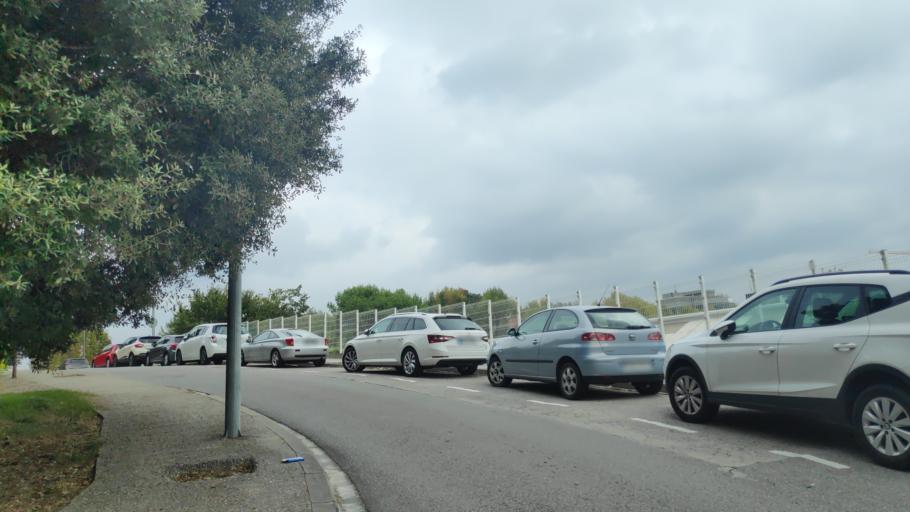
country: ES
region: Catalonia
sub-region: Provincia de Barcelona
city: Rubi
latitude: 41.4809
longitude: 2.0586
